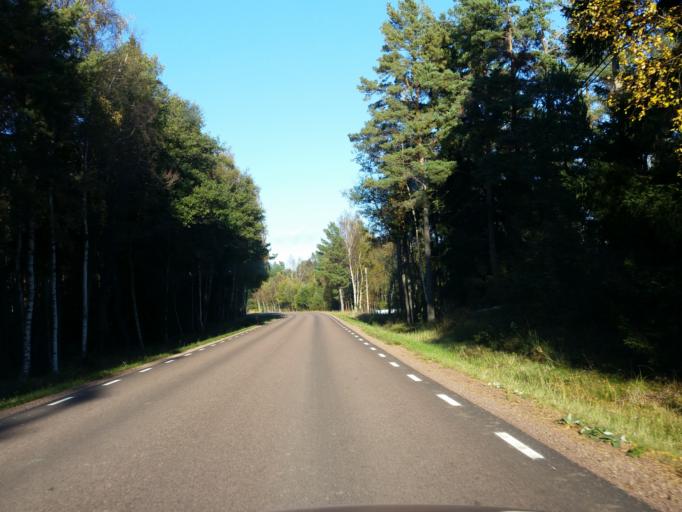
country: AX
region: Mariehamns stad
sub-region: Mariehamn
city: Mariehamn
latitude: 60.1386
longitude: 19.8582
